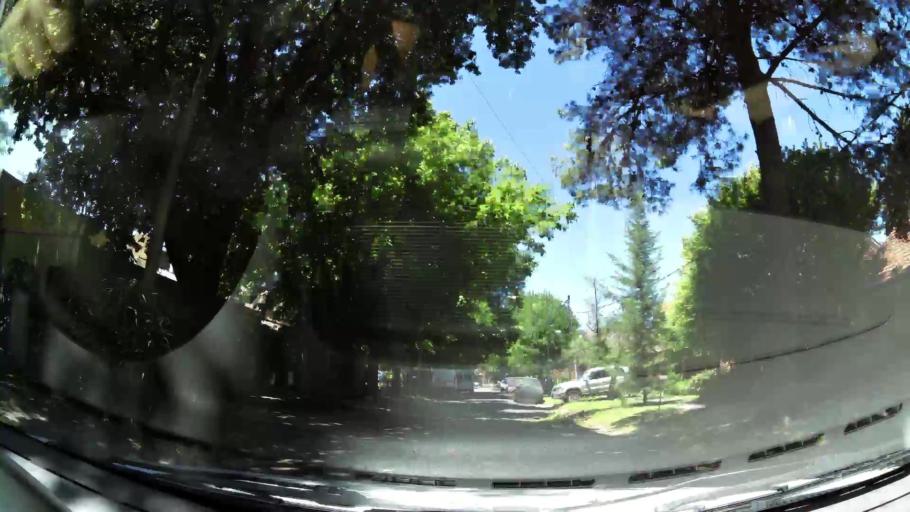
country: AR
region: Buenos Aires
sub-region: Partido de San Isidro
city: San Isidro
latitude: -34.4993
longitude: -58.5614
